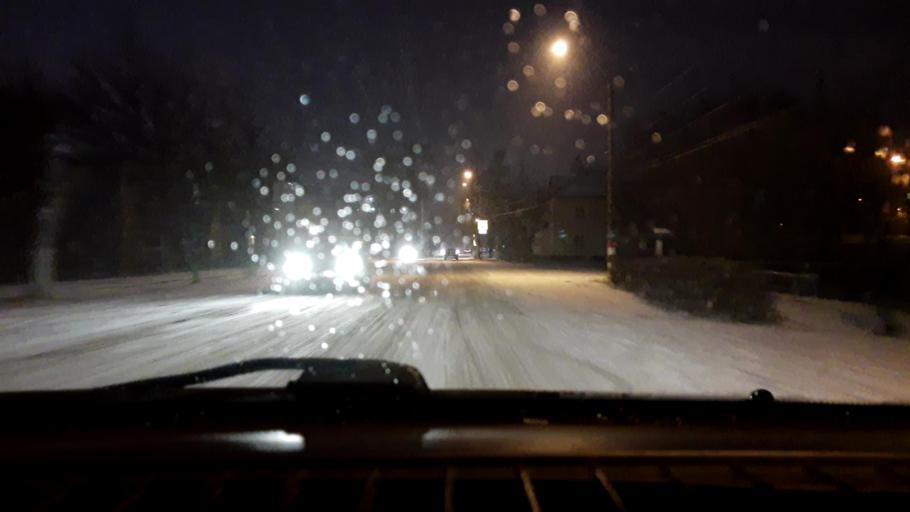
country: RU
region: Nizjnij Novgorod
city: Bor
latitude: 56.3353
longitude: 44.1131
